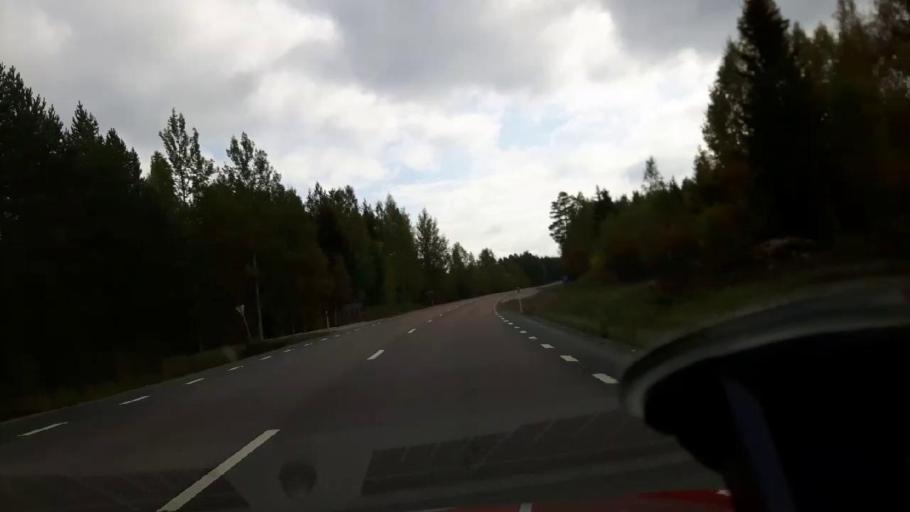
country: SE
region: Gaevleborg
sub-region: Bollnas Kommun
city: Kilafors
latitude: 61.2705
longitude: 16.5389
